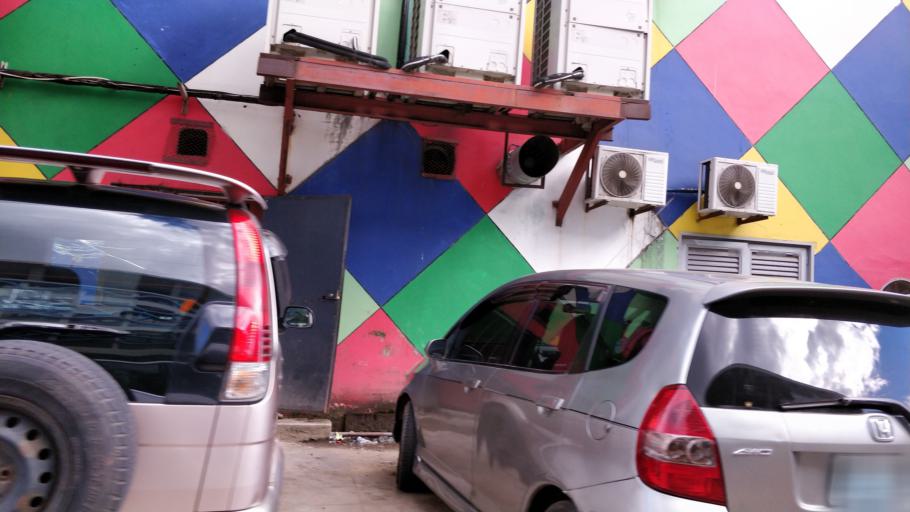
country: MZ
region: Maputo City
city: Maputo
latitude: -25.9756
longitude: 32.5732
